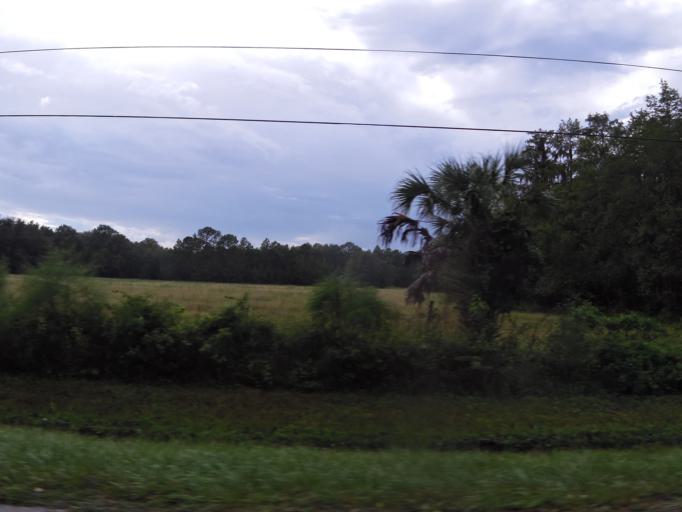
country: US
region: Florida
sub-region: Duval County
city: Baldwin
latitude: 30.3129
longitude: -81.8946
